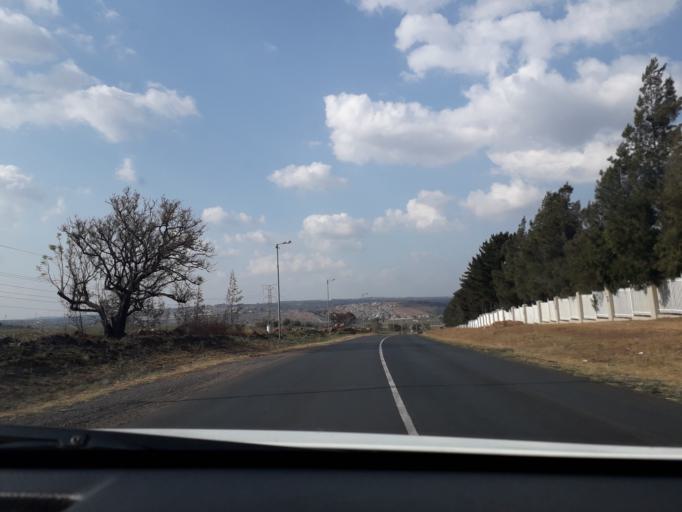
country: ZA
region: Gauteng
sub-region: City of Tshwane Metropolitan Municipality
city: Centurion
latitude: -25.8935
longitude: 28.2490
